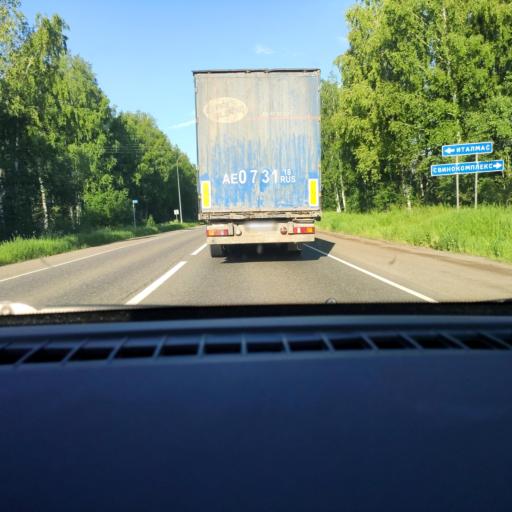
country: RU
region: Udmurtiya
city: Khokhryaki
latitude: 56.9205
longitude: 53.4830
